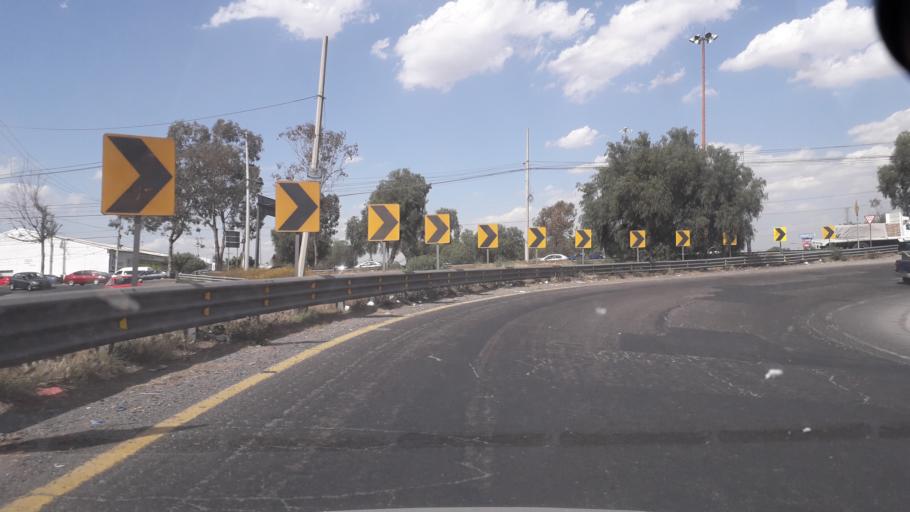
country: MX
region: Mexico
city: Ecatepec
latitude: 19.6132
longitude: -99.0418
